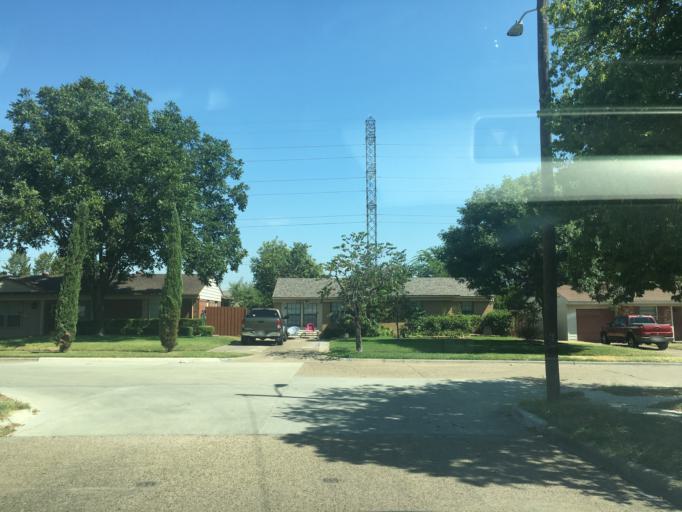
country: US
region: Texas
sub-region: Dallas County
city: Garland
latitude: 32.8549
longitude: -96.6691
